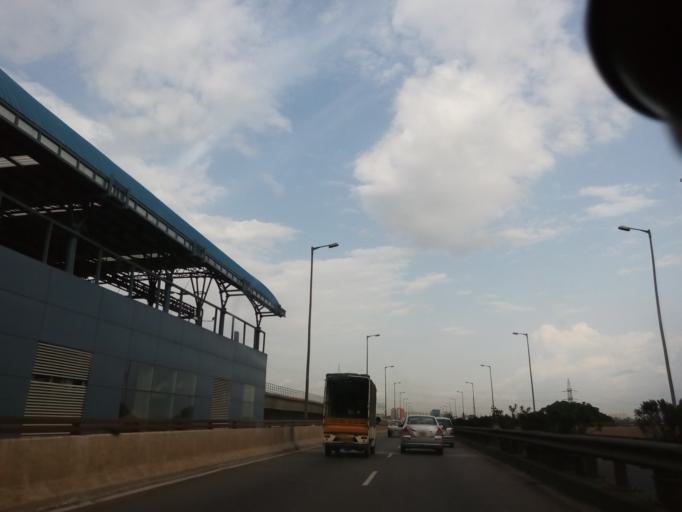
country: IN
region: Karnataka
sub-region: Bangalore Urban
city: Yelahanka
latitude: 13.0477
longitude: 77.5002
